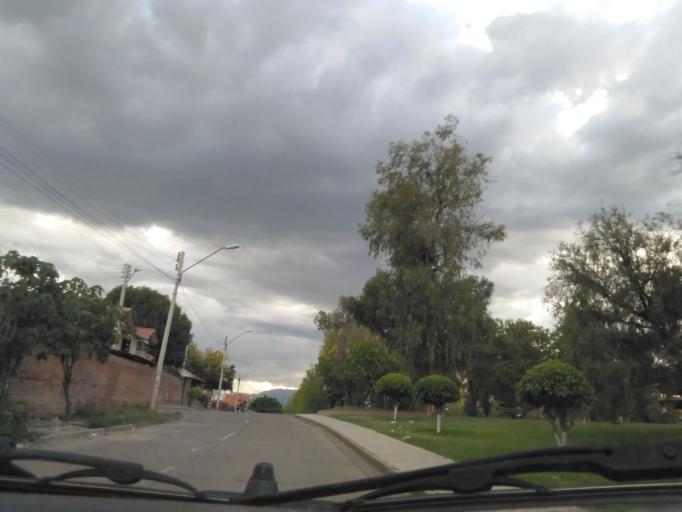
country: BO
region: Cochabamba
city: Cochabamba
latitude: -17.3702
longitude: -66.1706
